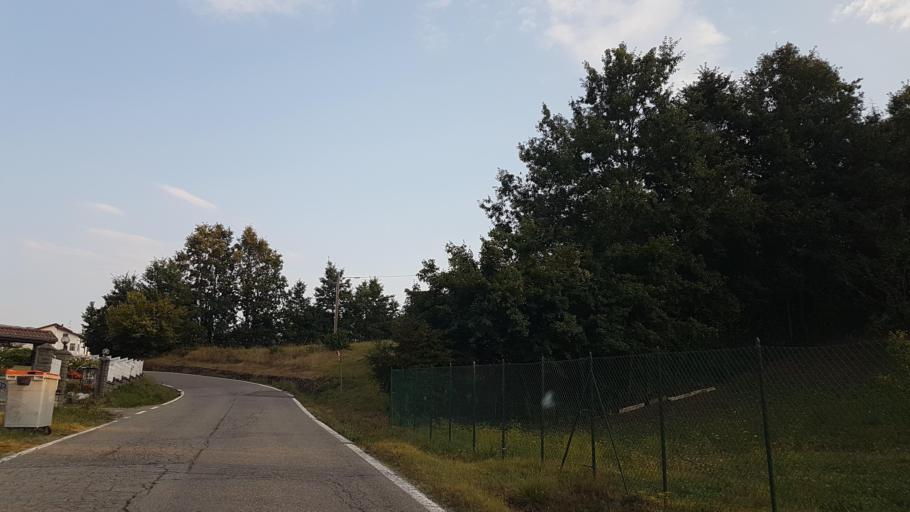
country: IT
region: Emilia-Romagna
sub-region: Provincia di Parma
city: Albareto
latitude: 44.4731
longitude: 9.7072
